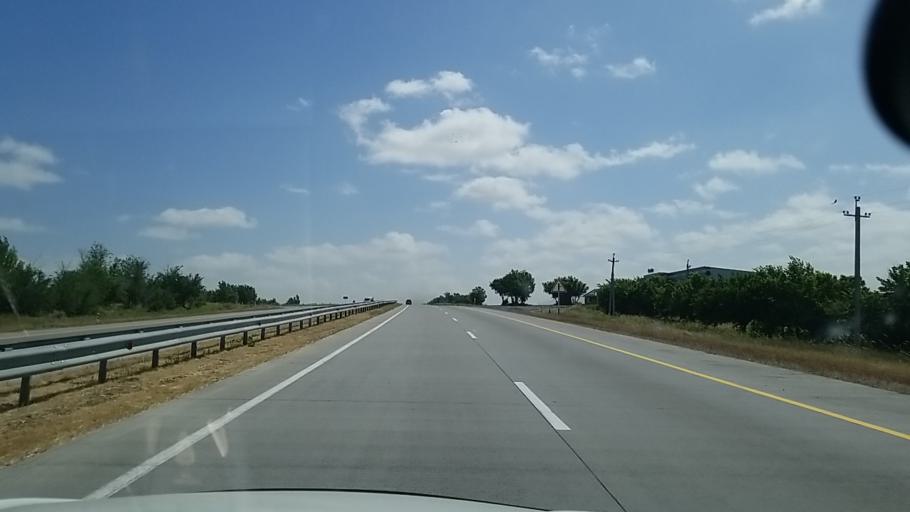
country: KZ
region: Ongtustik Qazaqstan
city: Sastobe
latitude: 42.4864
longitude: 69.9344
